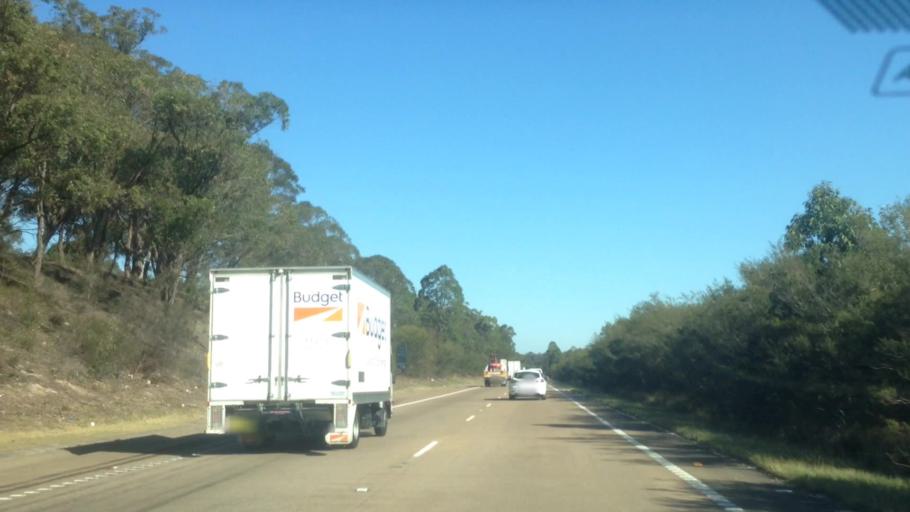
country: AU
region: New South Wales
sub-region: Wyong Shire
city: Charmhaven
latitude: -33.1614
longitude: 151.4696
